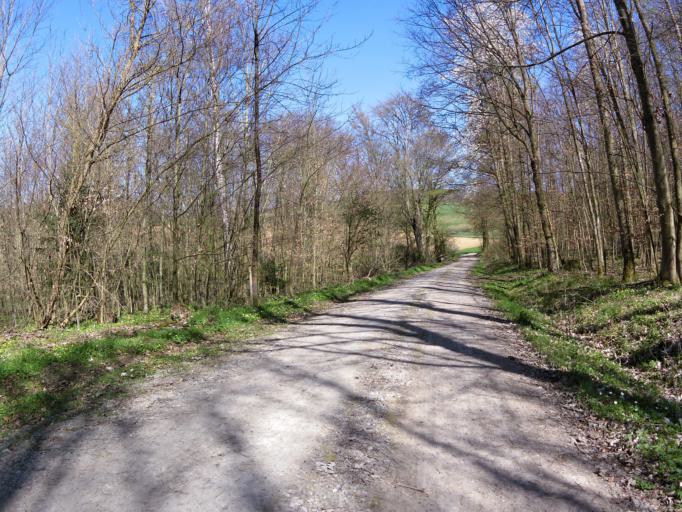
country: DE
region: Bavaria
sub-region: Regierungsbezirk Unterfranken
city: Rottendorf
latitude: 49.8209
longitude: 10.0485
